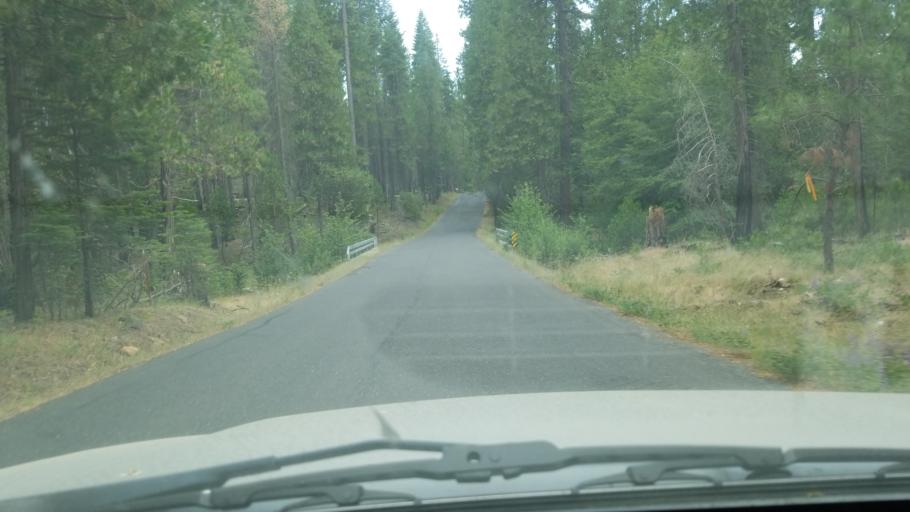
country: US
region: California
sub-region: Mariposa County
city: Yosemite Valley
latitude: 37.8328
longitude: -119.8499
